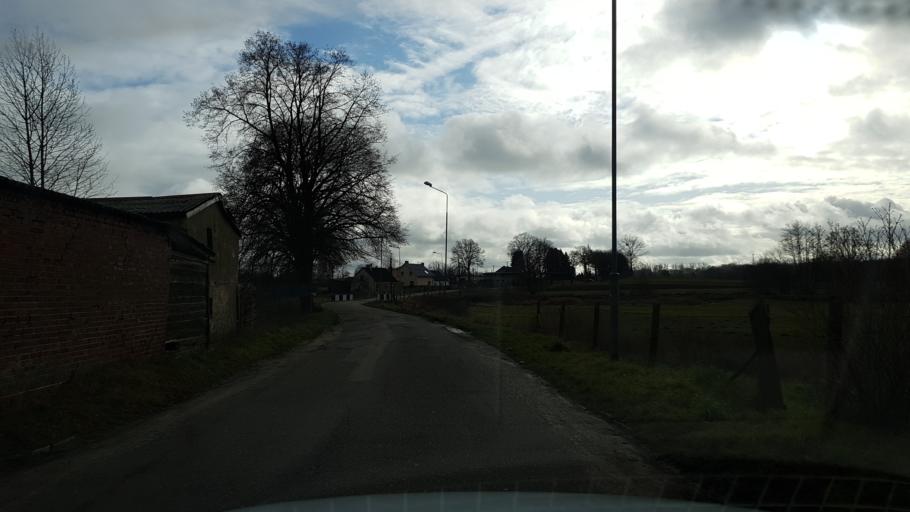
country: PL
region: West Pomeranian Voivodeship
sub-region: Powiat swidwinski
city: Rabino
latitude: 53.7739
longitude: 15.9679
